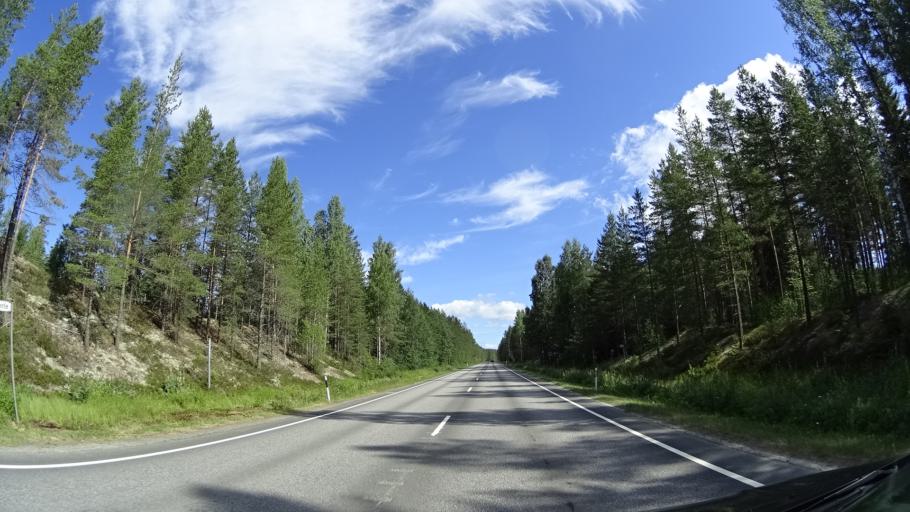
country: FI
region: Pirkanmaa
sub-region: Luoteis-Pirkanmaa
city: Kihnioe
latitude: 62.1166
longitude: 23.1049
